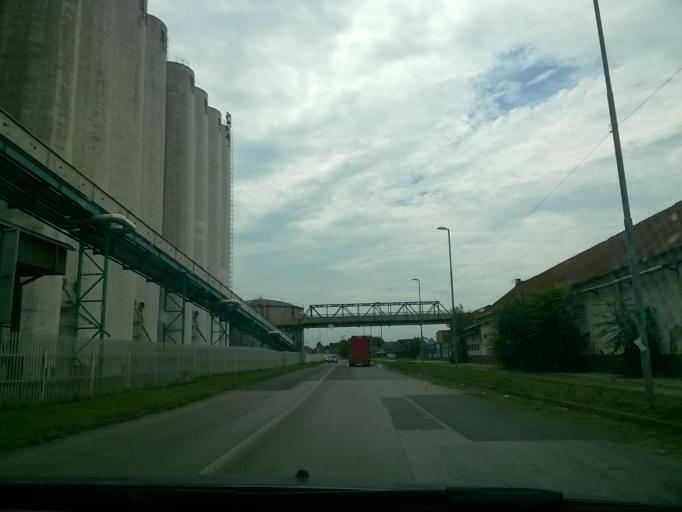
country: RS
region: Autonomna Pokrajina Vojvodina
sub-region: Srednjebanatski Okrug
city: Zrenjanin
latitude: 45.3848
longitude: 20.4147
